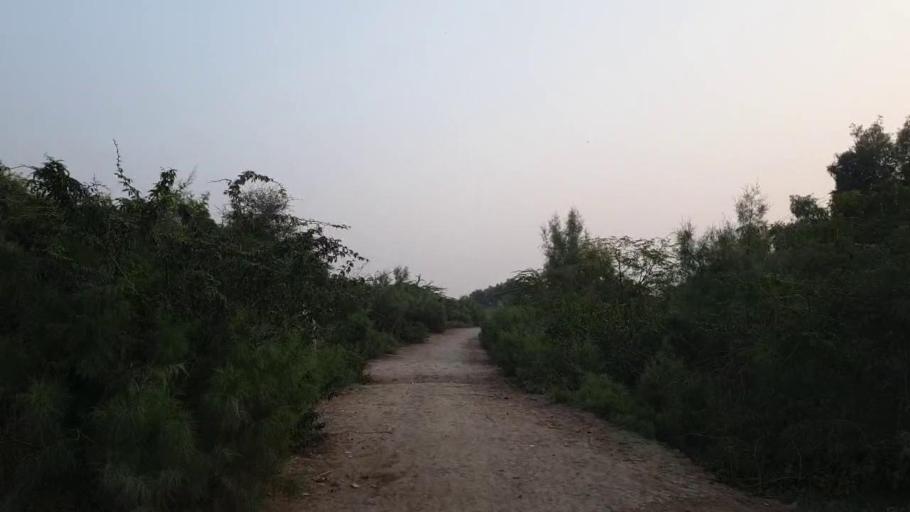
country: PK
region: Sindh
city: Bhan
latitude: 26.5315
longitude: 67.7063
